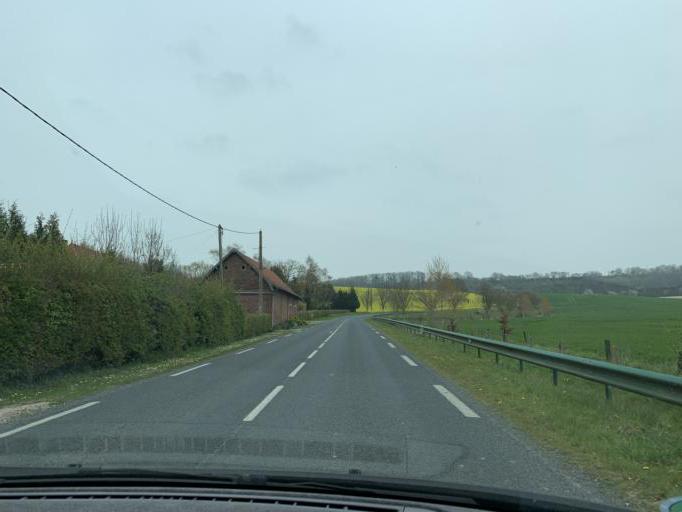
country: FR
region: Haute-Normandie
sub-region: Departement de la Seine-Maritime
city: Londinieres
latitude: 49.8404
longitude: 1.4467
